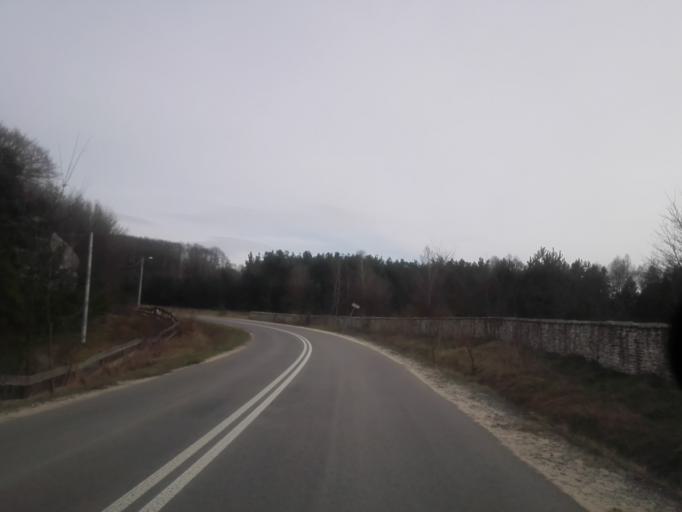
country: PL
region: Silesian Voivodeship
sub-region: Powiat czestochowski
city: Potok Zloty
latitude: 50.7021
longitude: 19.3596
